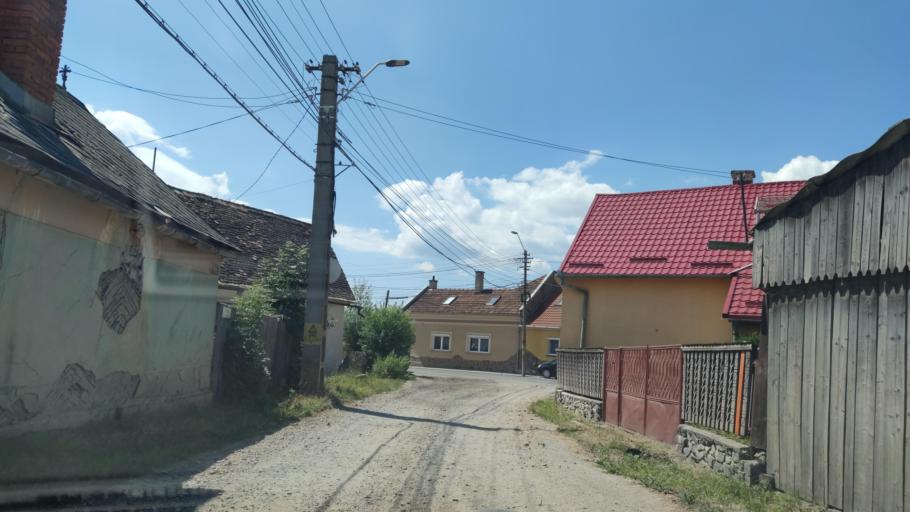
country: RO
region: Harghita
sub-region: Municipiul Gheorgheni
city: Gheorgheni
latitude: 46.7181
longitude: 25.6031
